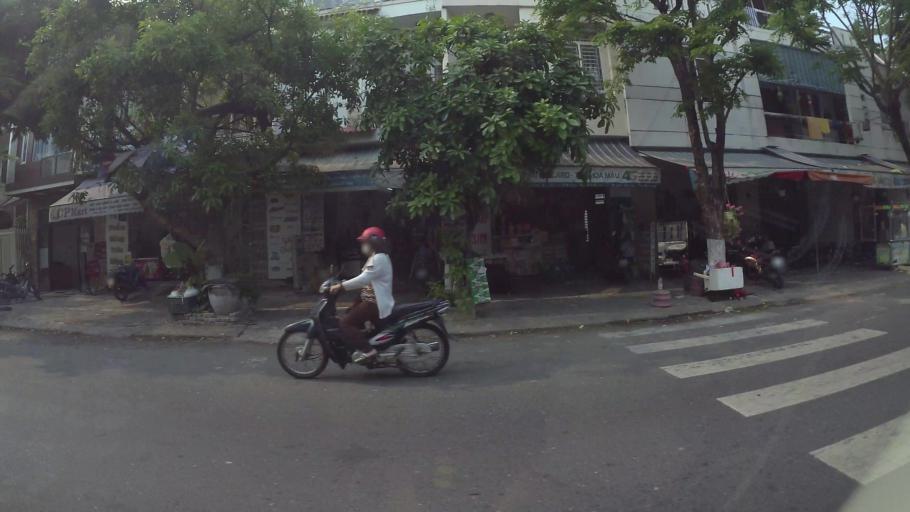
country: VN
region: Da Nang
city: Son Tra
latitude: 16.0453
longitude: 108.2182
